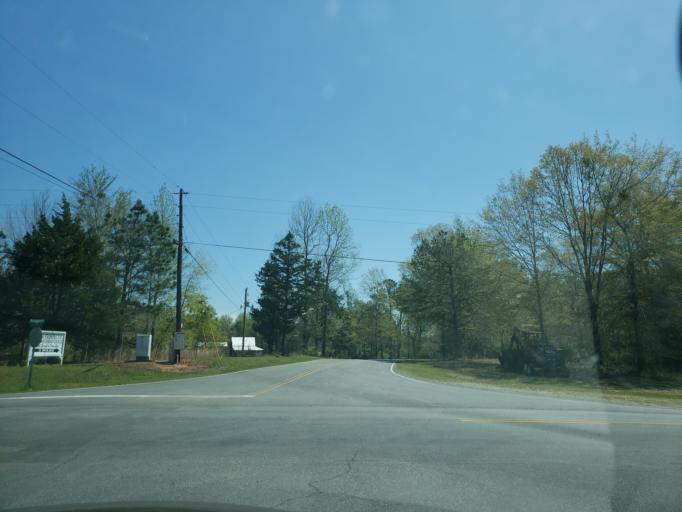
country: US
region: Alabama
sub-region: Elmore County
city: Tallassee
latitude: 32.6669
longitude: -85.8532
